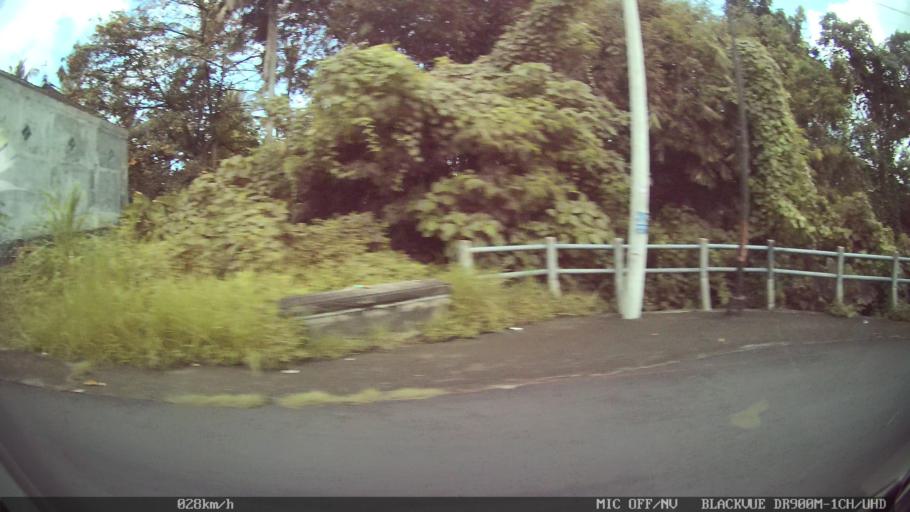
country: ID
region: Bali
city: Klungkung
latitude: -8.5374
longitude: 115.3934
